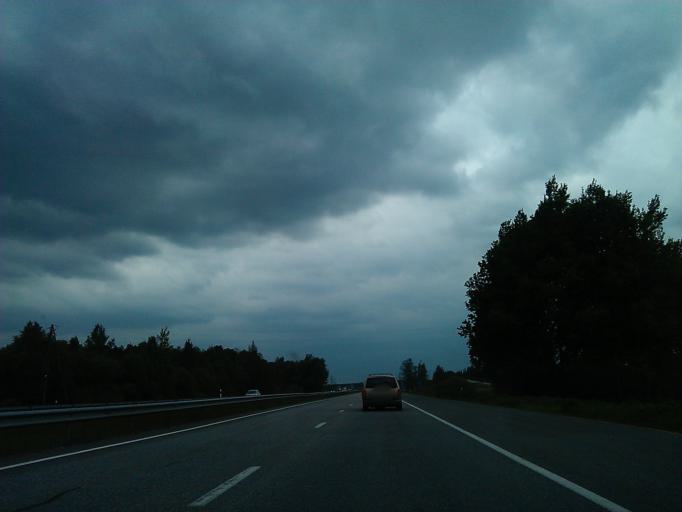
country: LV
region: Marupe
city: Marupe
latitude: 56.8394
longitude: 24.0481
